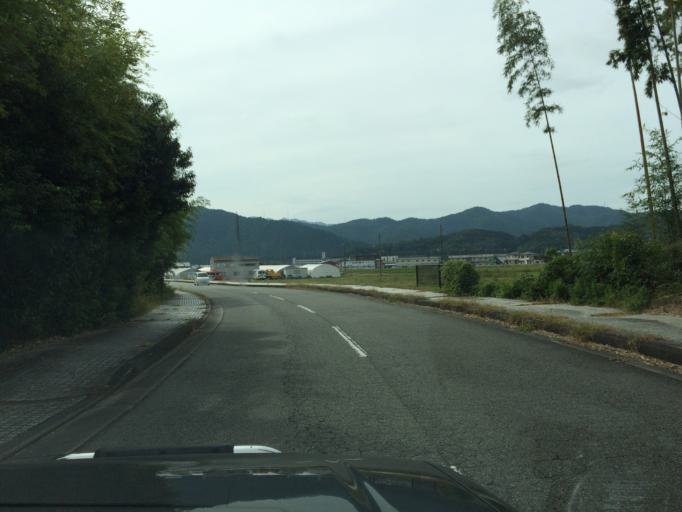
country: JP
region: Hyogo
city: Sasayama
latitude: 35.0744
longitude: 135.2135
